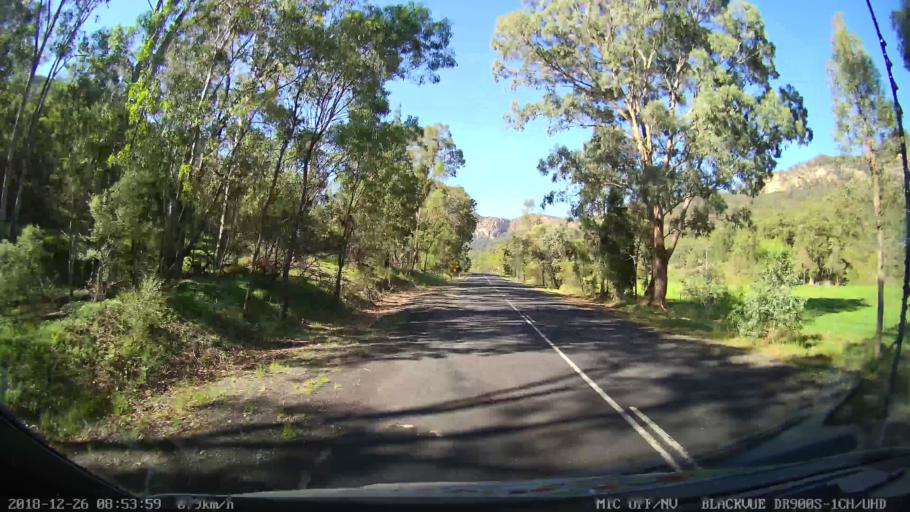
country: AU
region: New South Wales
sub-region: Mid-Western Regional
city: Kandos
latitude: -32.6104
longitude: 150.0750
